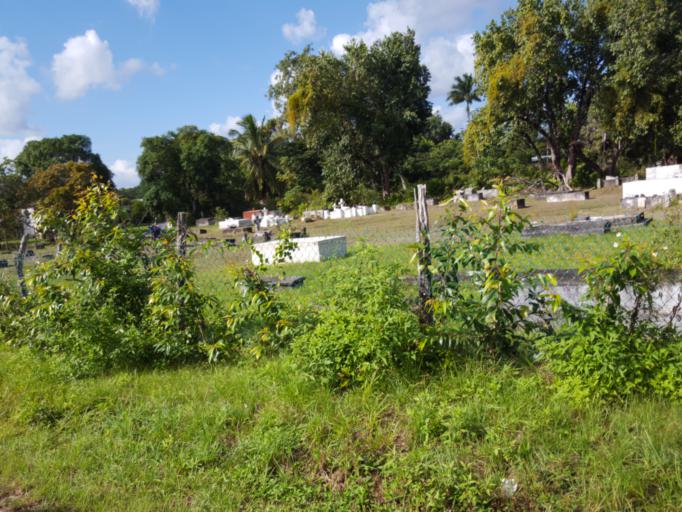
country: BZ
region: Belize
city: Belize City
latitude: 17.5675
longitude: -88.4030
